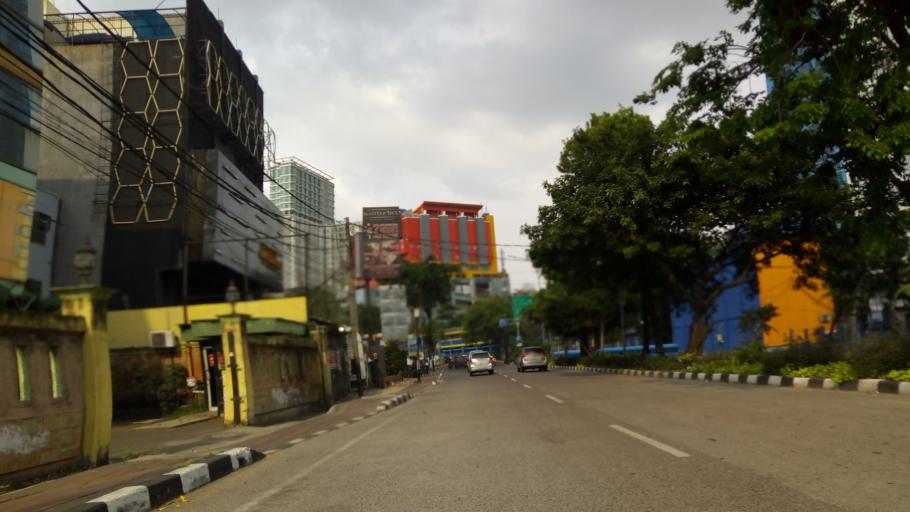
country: ID
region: Jakarta Raya
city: Jakarta
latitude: -6.1485
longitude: 106.8330
